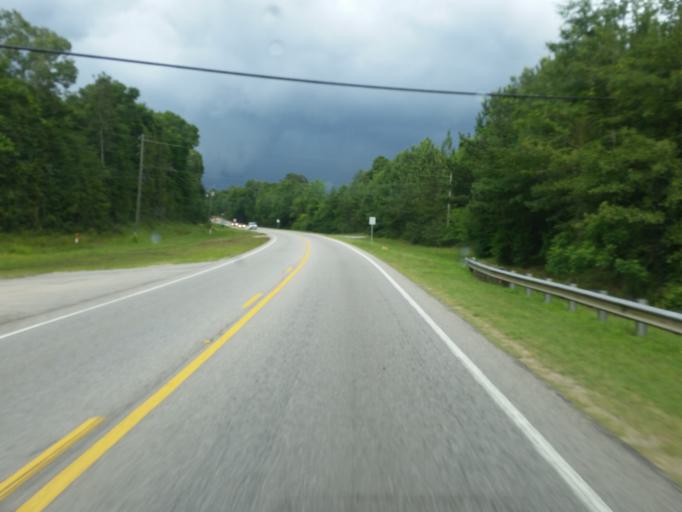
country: US
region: Mississippi
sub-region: Jackson County
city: Hurley
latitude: 30.7996
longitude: -88.3309
